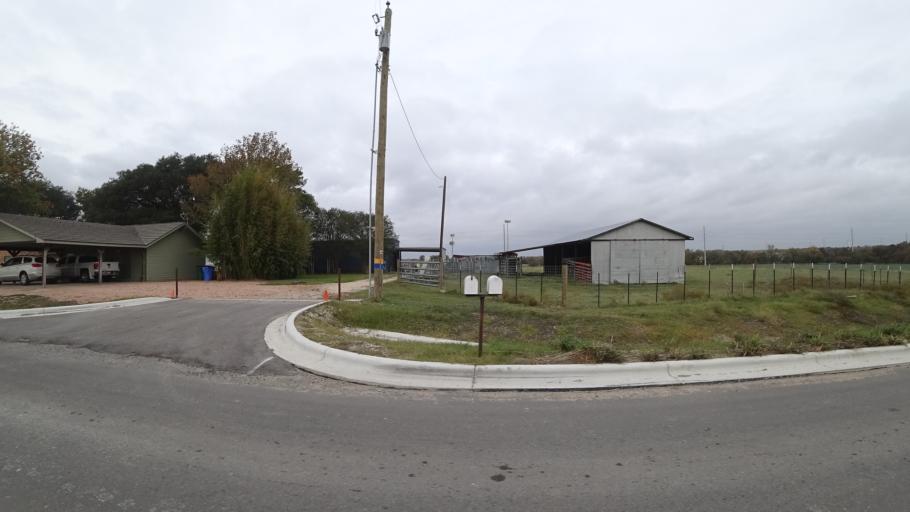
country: US
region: Texas
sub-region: Travis County
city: Pflugerville
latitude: 30.4214
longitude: -97.5780
